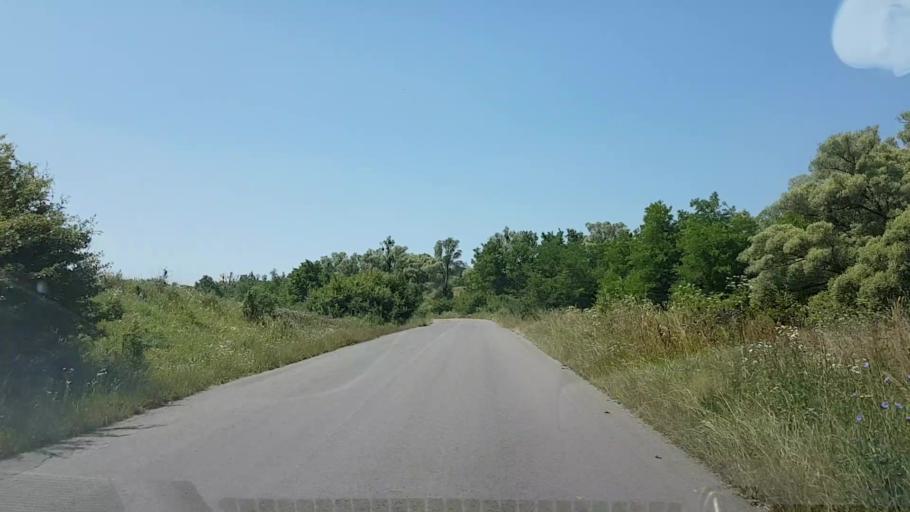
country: RO
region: Brasov
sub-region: Comuna Cincu
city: Cincu
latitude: 45.9500
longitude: 24.7837
